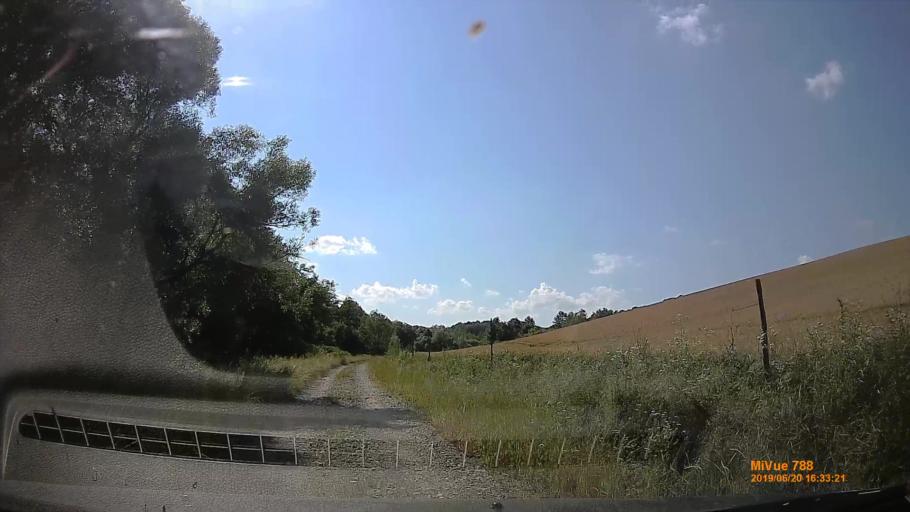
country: HU
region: Baranya
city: Buekkoesd
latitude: 46.1730
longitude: 18.0476
